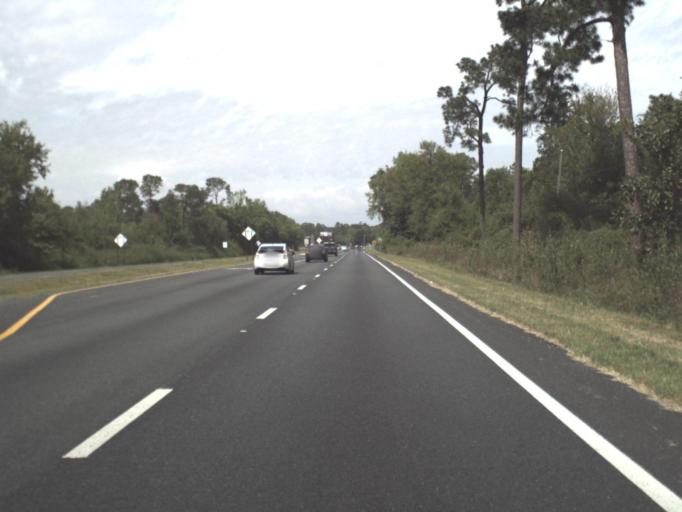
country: US
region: Florida
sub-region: Santa Rosa County
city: Pace
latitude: 30.5855
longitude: -87.1779
